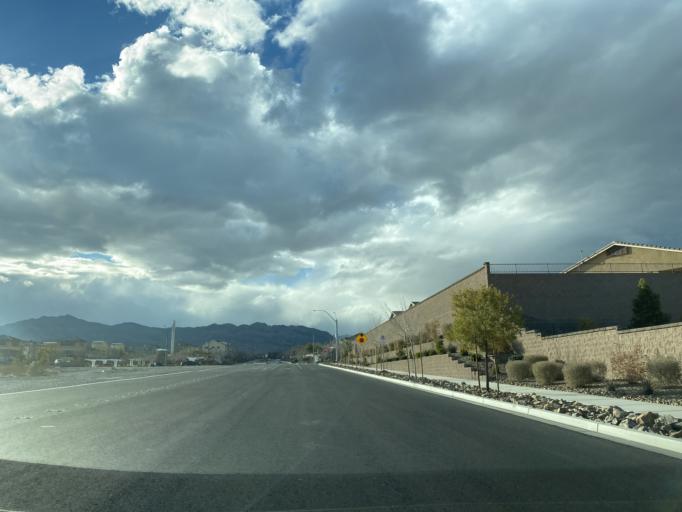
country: US
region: Nevada
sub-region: Clark County
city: Summerlin South
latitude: 36.2922
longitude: -115.3133
